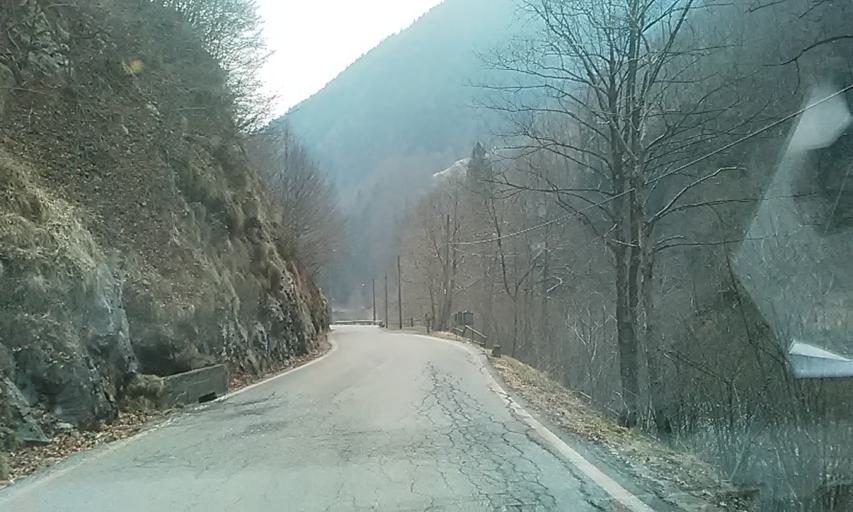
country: IT
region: Piedmont
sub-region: Provincia di Vercelli
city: Fobello
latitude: 45.8938
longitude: 8.1537
